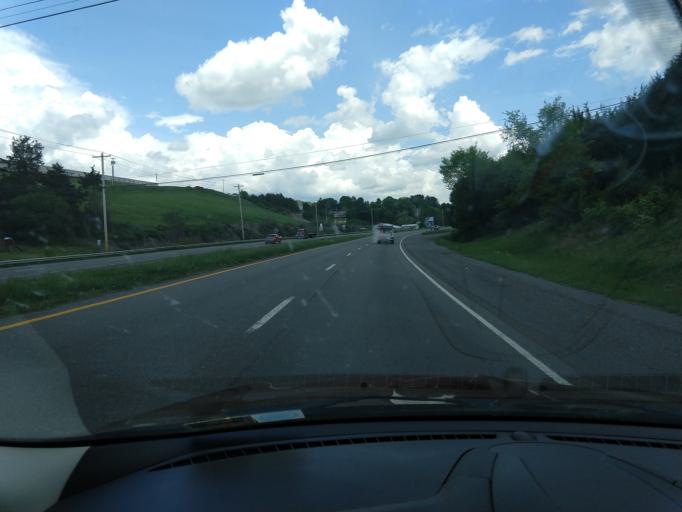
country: US
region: Virginia
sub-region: Tazewell County
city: Claypool Hill
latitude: 37.0372
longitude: -81.7950
